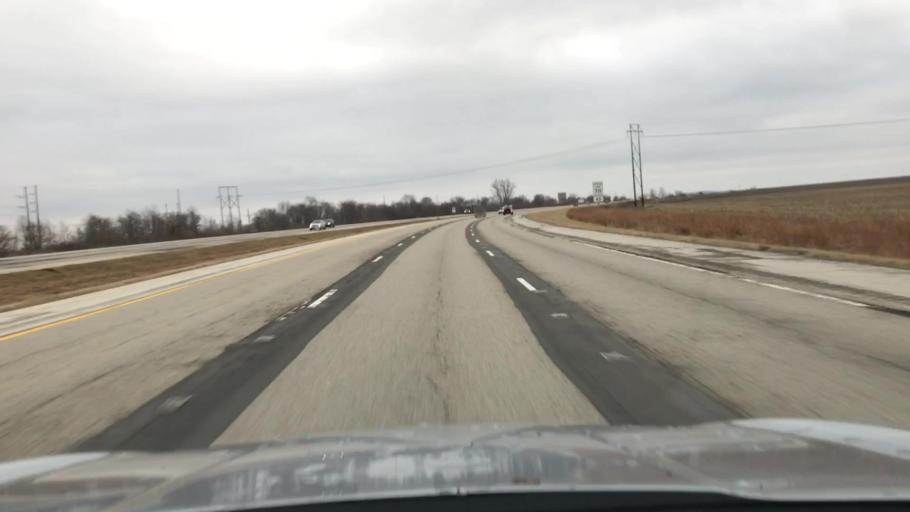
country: US
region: Illinois
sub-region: Logan County
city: Lincoln
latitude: 40.1022
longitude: -89.4168
